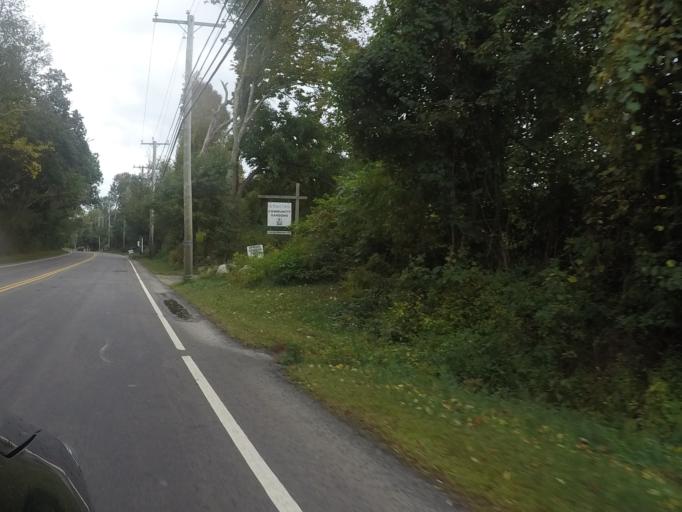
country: US
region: Massachusetts
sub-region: Bristol County
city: Smith Mills
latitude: 41.6148
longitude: -71.0011
